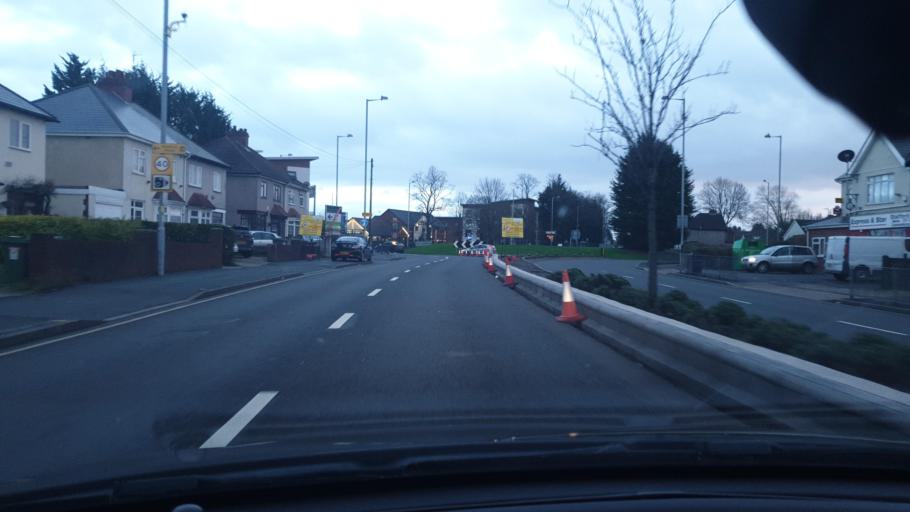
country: GB
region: England
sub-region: Wolverhampton
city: Wolverhampton
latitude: 52.6116
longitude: -2.1312
